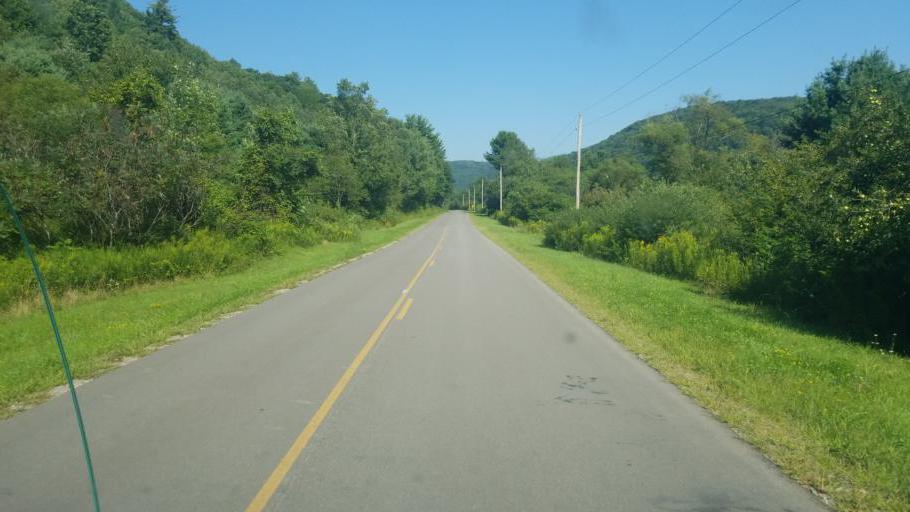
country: US
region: New York
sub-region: Allegany County
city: Wellsville
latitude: 42.0136
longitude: -78.0146
